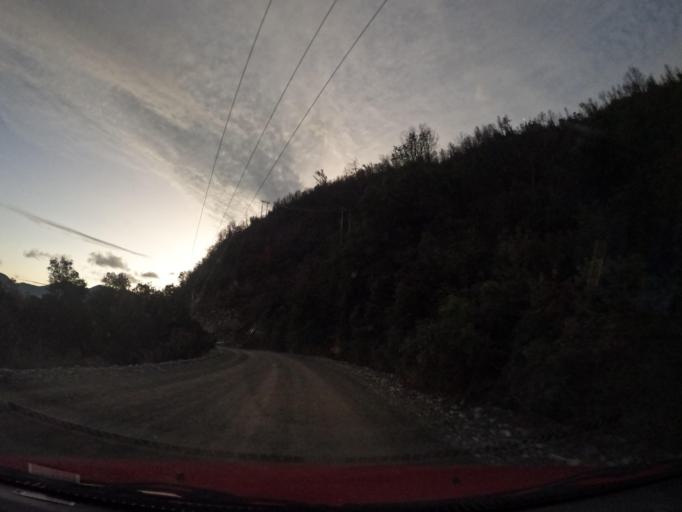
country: CL
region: Maule
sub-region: Provincia de Linares
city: Colbun
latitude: -35.8579
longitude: -71.2110
